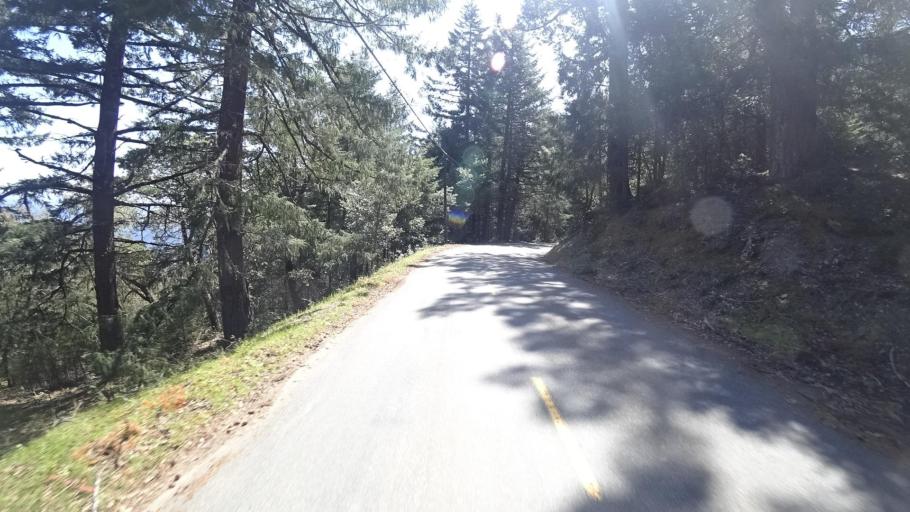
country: US
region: California
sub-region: Humboldt County
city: Redway
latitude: 40.0948
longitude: -123.6797
